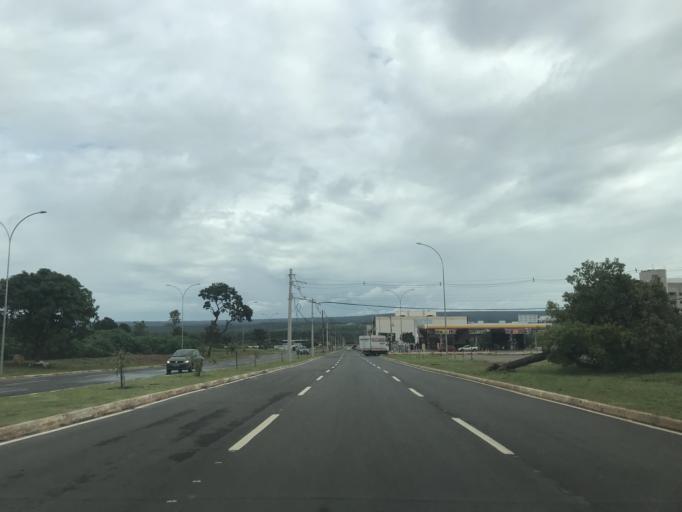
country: BR
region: Federal District
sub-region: Brasilia
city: Brasilia
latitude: -15.7482
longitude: -47.9146
